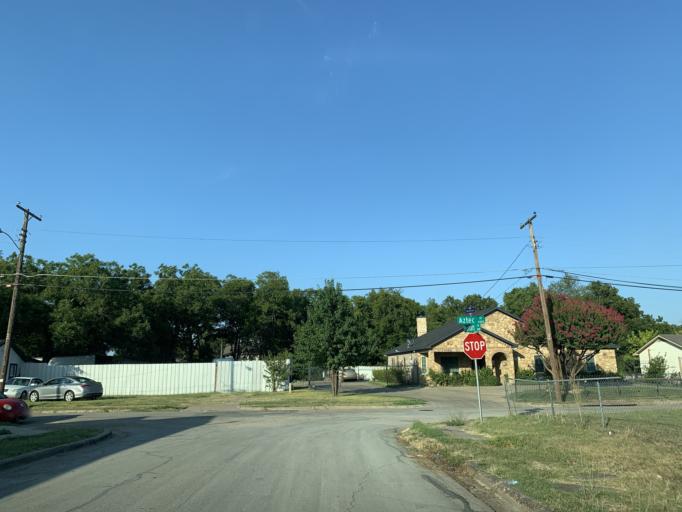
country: US
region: Texas
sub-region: Dallas County
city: Hutchins
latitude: 32.7006
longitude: -96.7818
